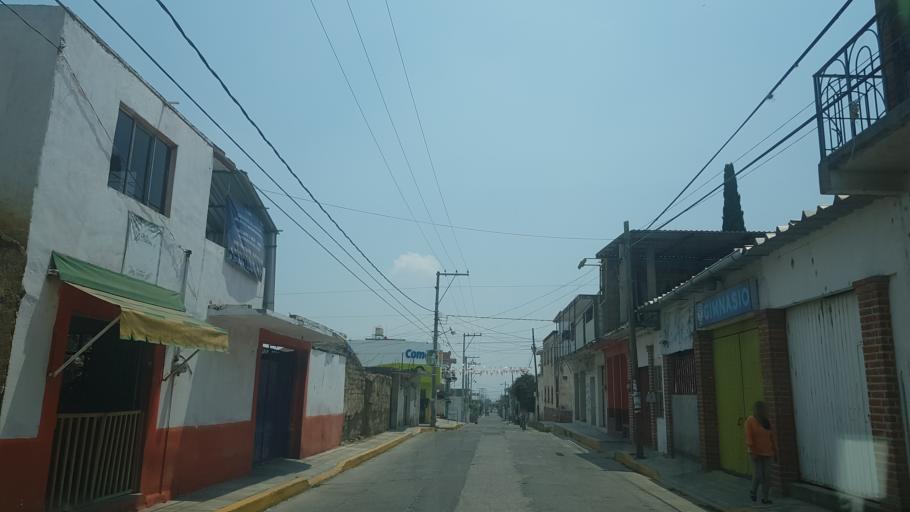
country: MX
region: Puebla
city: San Andres Calpan
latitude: 19.1039
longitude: -98.4591
